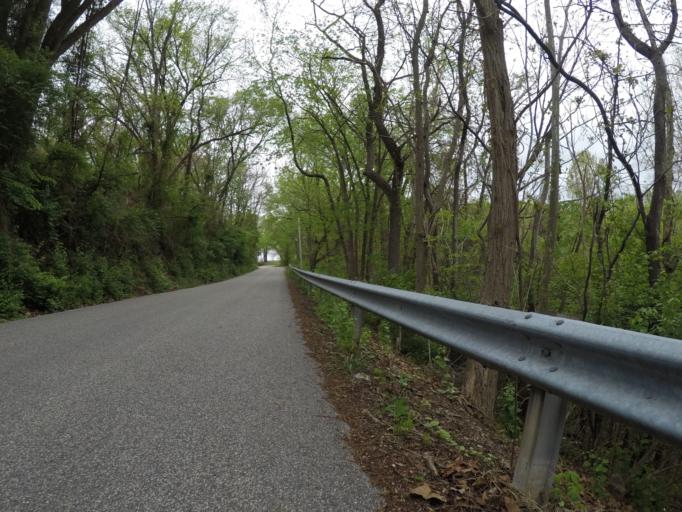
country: US
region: West Virginia
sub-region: Cabell County
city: Barboursville
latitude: 38.4024
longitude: -82.2714
